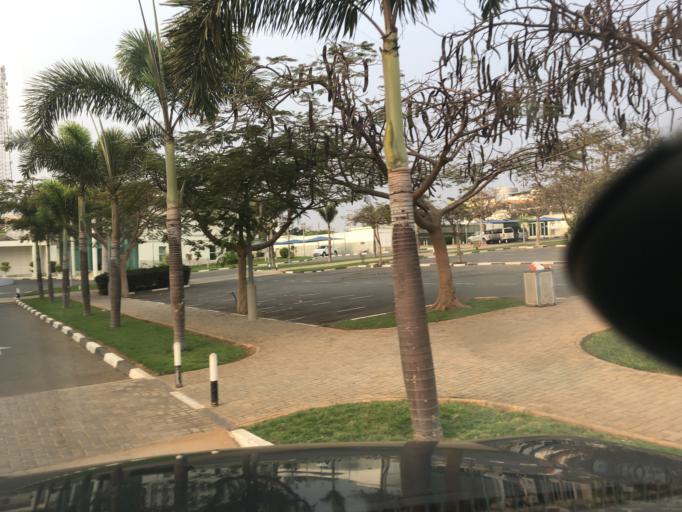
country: AO
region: Luanda
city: Luanda
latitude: -8.8894
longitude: 13.1817
